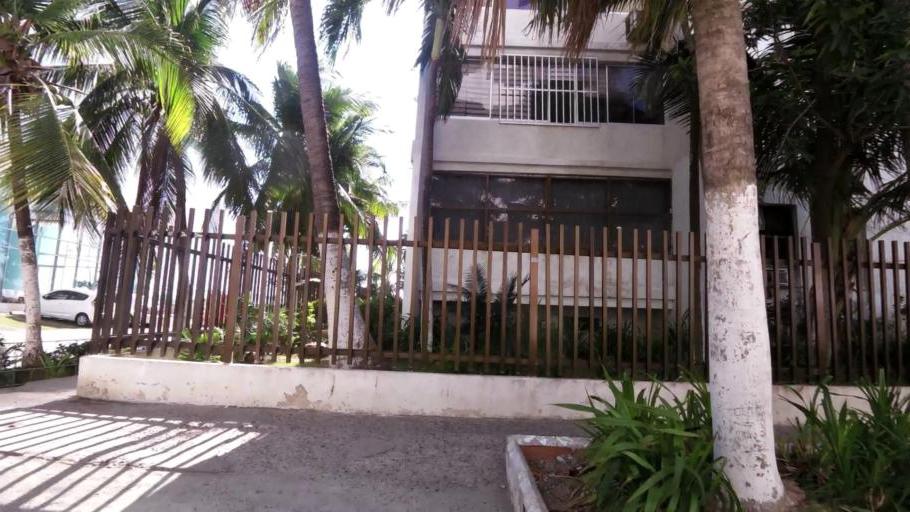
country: CO
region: Bolivar
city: Cartagena
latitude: 10.3954
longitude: -75.5628
